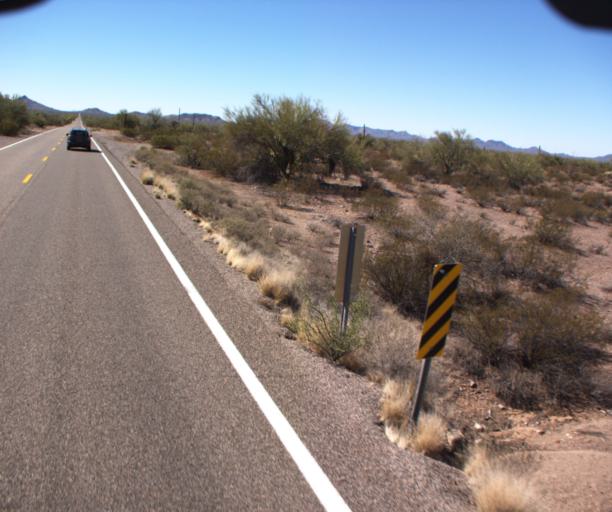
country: US
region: Arizona
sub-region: Pima County
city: Ajo
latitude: 32.1580
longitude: -112.7644
